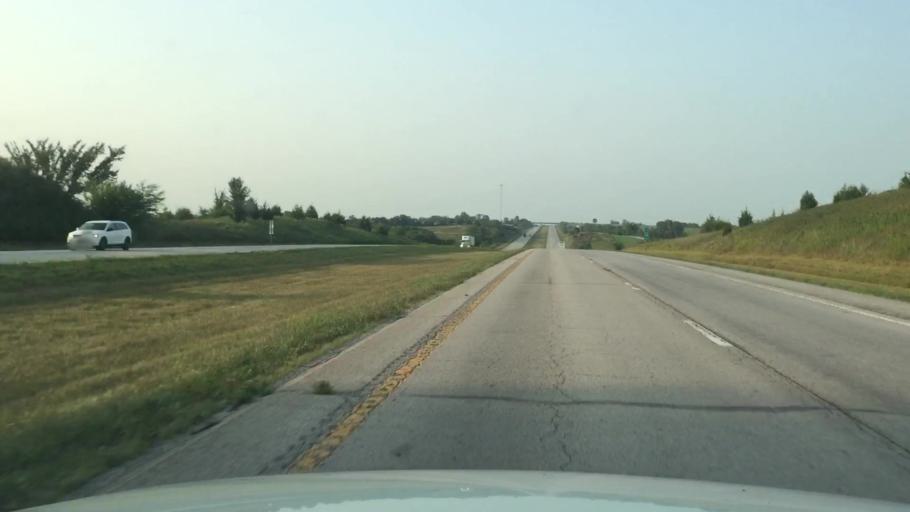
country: US
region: Iowa
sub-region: Decatur County
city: Lamoni
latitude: 40.4983
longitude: -93.9678
